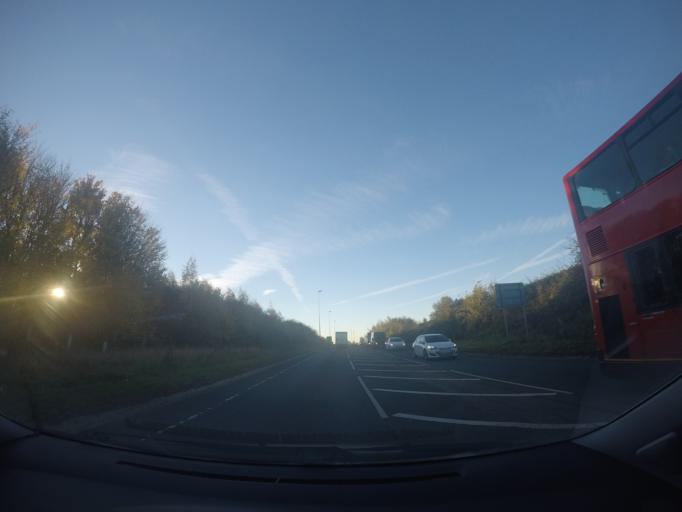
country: GB
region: England
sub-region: City of York
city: Copmanthorpe
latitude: 53.9384
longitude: -1.1449
